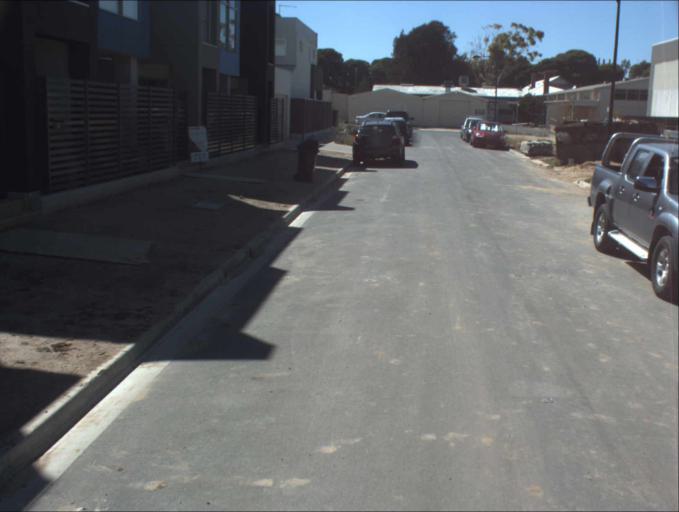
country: AU
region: South Australia
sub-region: Port Adelaide Enfield
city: Enfield
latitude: -34.8596
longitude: 138.6203
